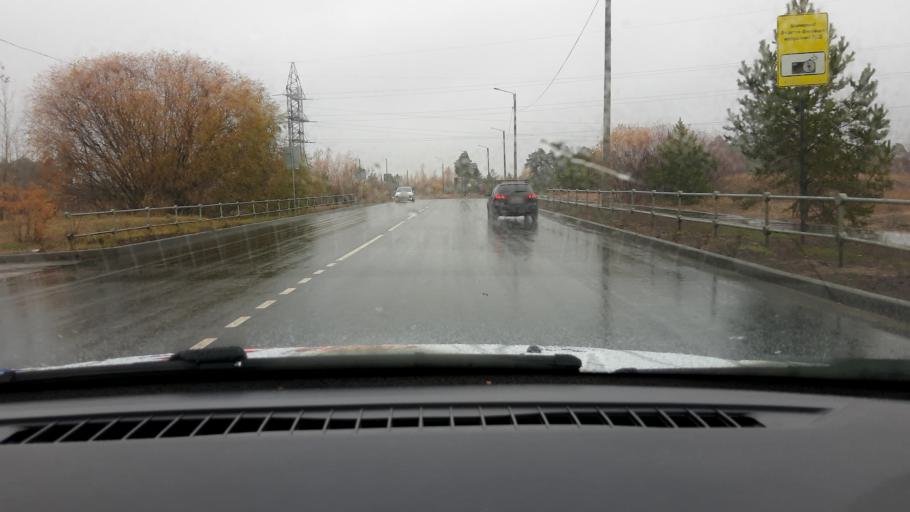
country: RU
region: Nizjnij Novgorod
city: Dzerzhinsk
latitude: 56.2349
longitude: 43.4083
